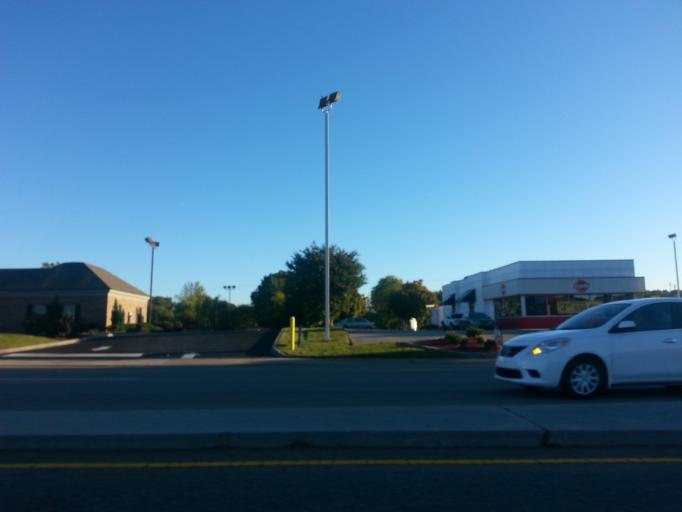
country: US
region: Tennessee
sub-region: Knox County
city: Knoxville
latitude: 35.9744
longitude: -83.9760
